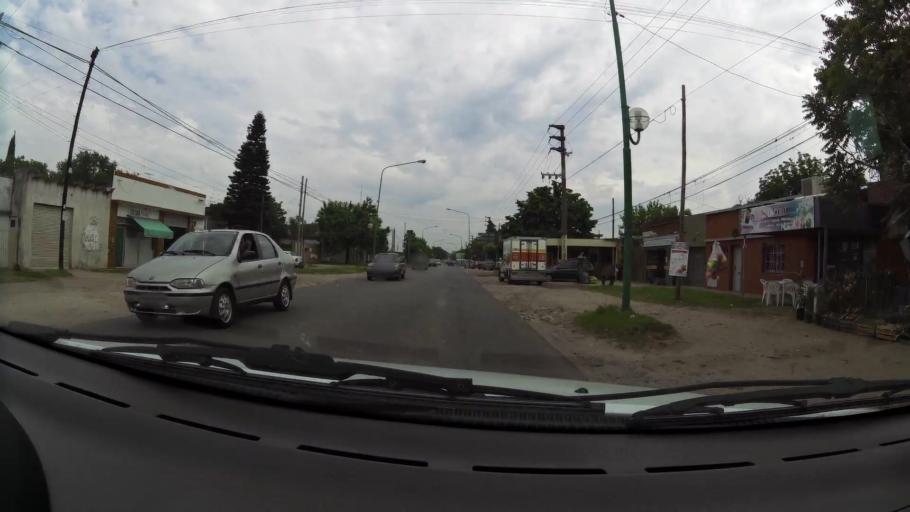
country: AR
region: Buenos Aires
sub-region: Partido de La Plata
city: La Plata
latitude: -34.9256
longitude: -58.0048
